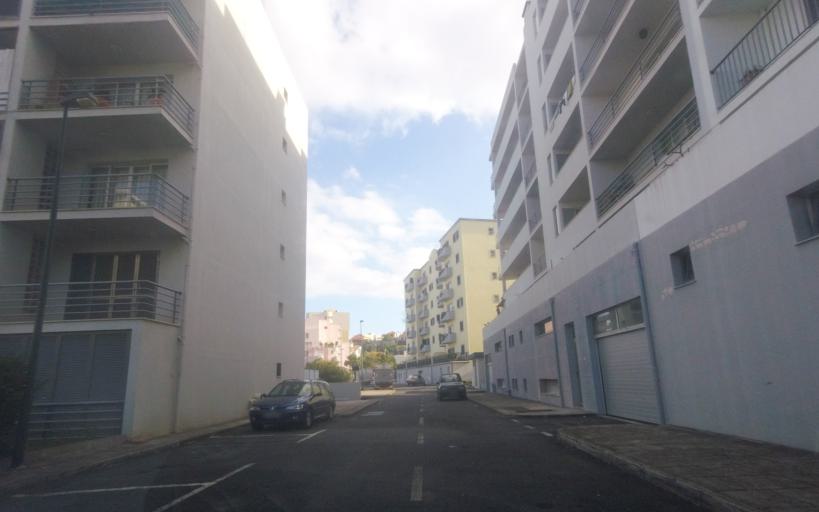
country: PT
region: Madeira
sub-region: Funchal
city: Funchal
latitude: 32.6490
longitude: -16.9326
